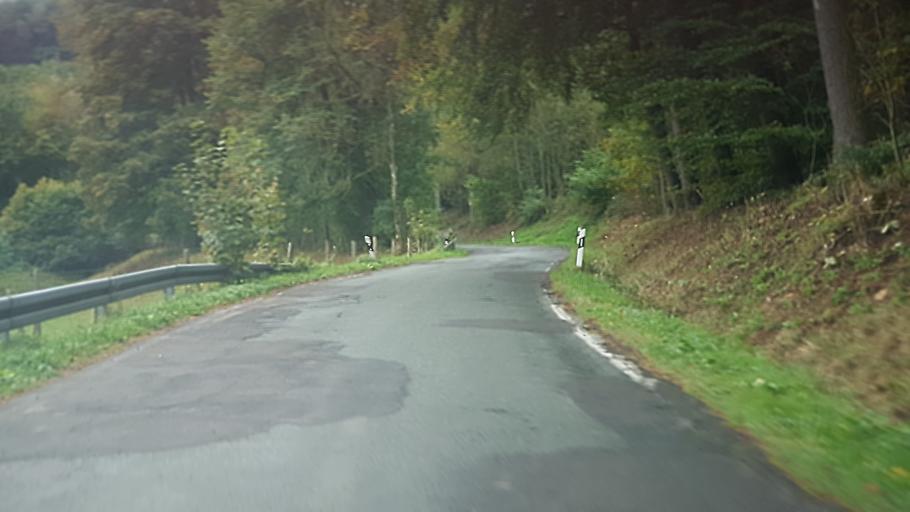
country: DE
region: North Rhine-Westphalia
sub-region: Regierungsbezirk Arnsberg
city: Herscheid
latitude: 51.1921
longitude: 7.6940
